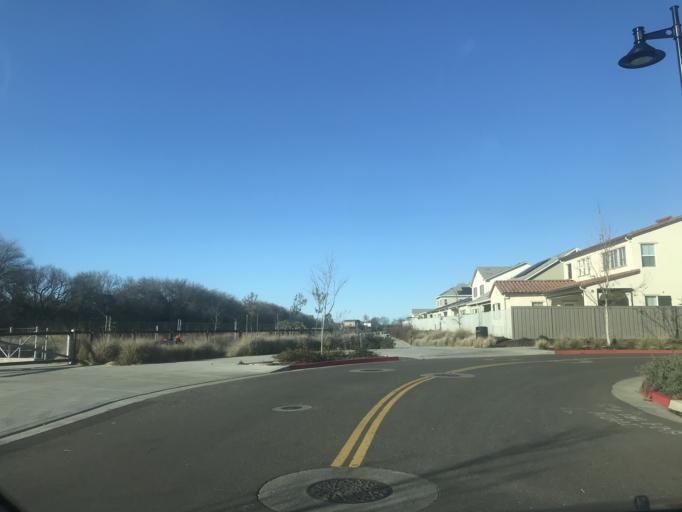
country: US
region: California
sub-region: Yolo County
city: Davis
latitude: 38.5663
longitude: -121.7443
